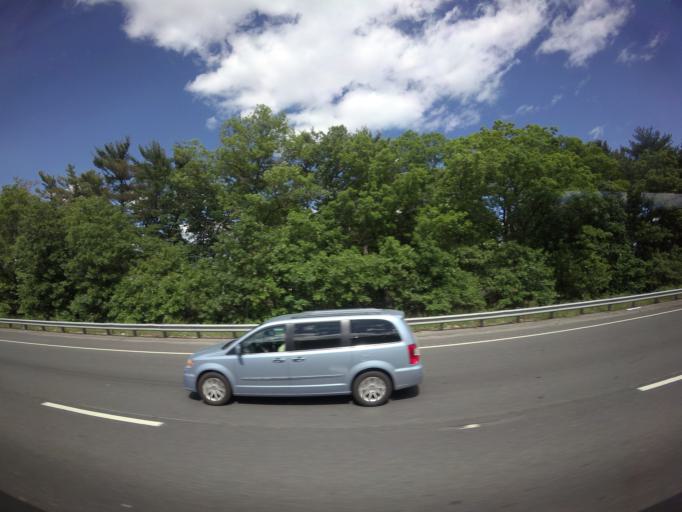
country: US
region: Massachusetts
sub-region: Middlesex County
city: Wilmington
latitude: 42.5595
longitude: -71.1411
